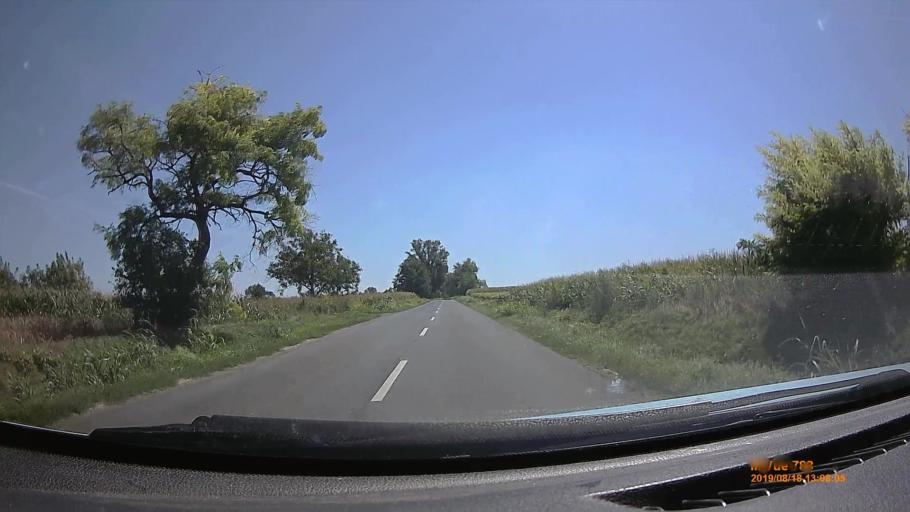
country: HU
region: Fejer
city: Kaloz
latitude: 46.9431
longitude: 18.4991
